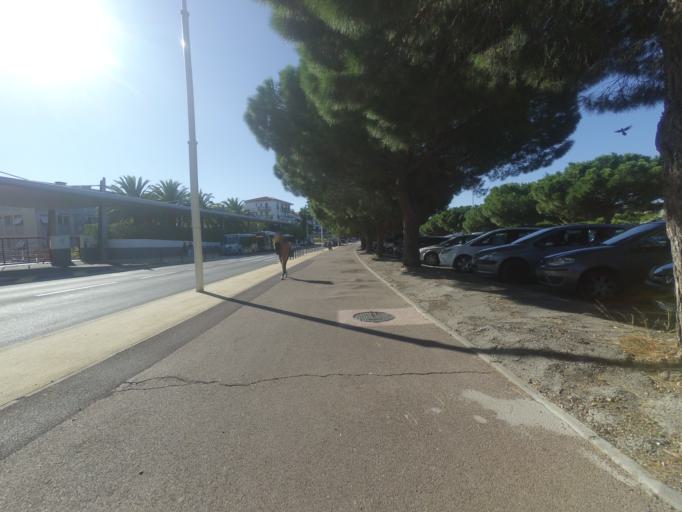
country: FR
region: Languedoc-Roussillon
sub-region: Departement des Pyrenees-Orientales
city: Perpignan
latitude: 42.6778
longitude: 2.9050
